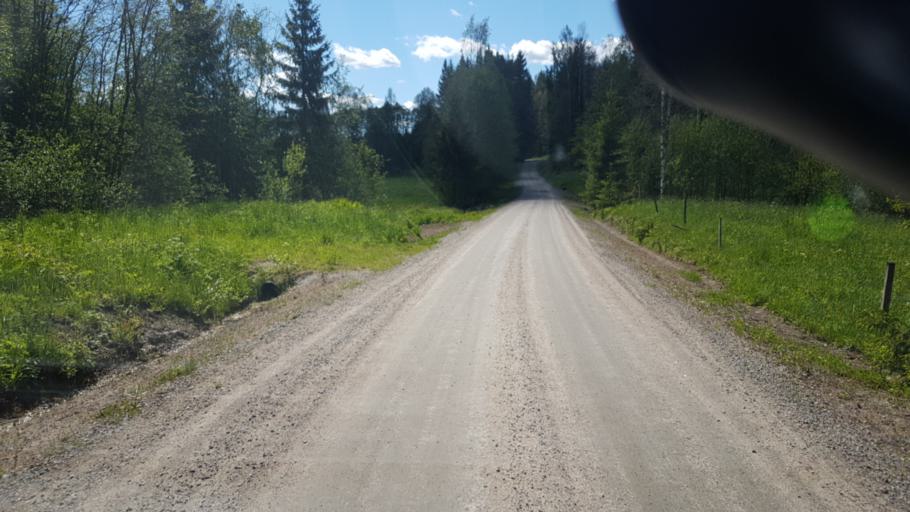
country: SE
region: Vaermland
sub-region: Arvika Kommun
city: Arvika
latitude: 59.6842
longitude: 12.7727
